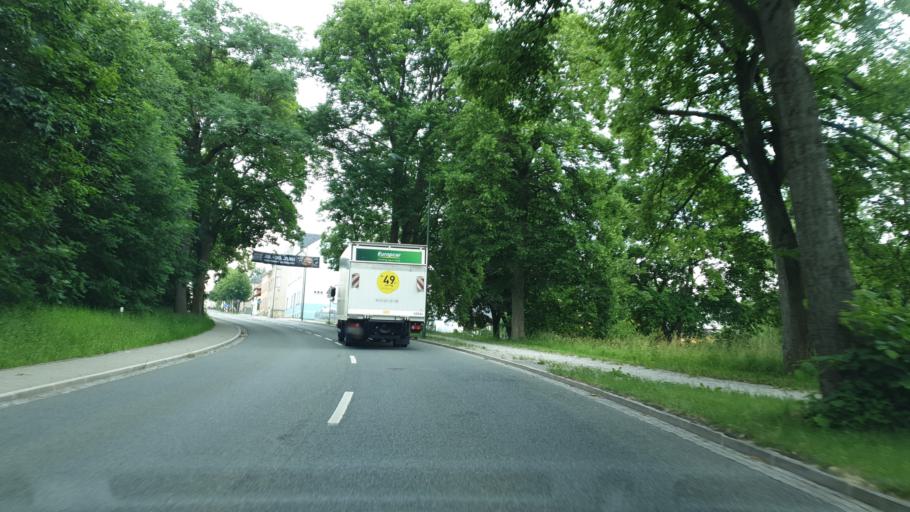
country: DE
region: Saxony
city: Auerbach
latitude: 50.5046
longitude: 12.4130
